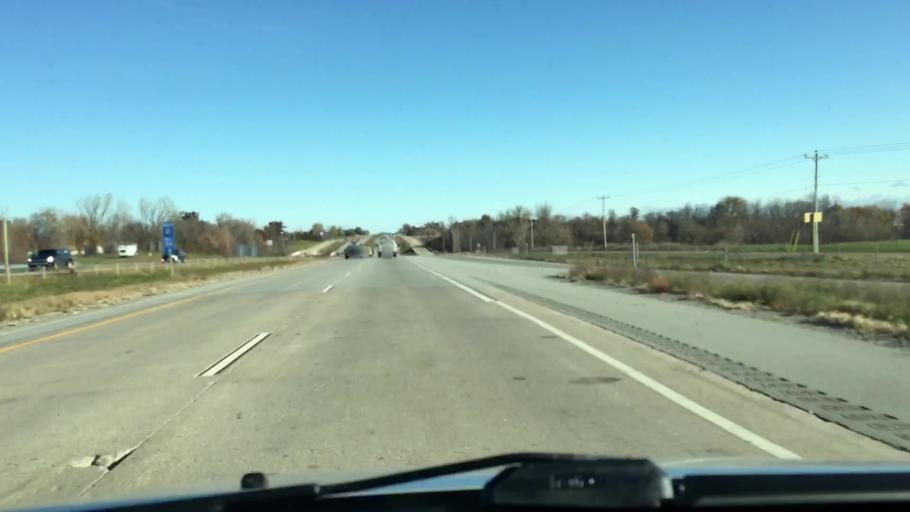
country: US
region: Wisconsin
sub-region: Brown County
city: Wrightstown
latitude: 44.3508
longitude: -88.1919
